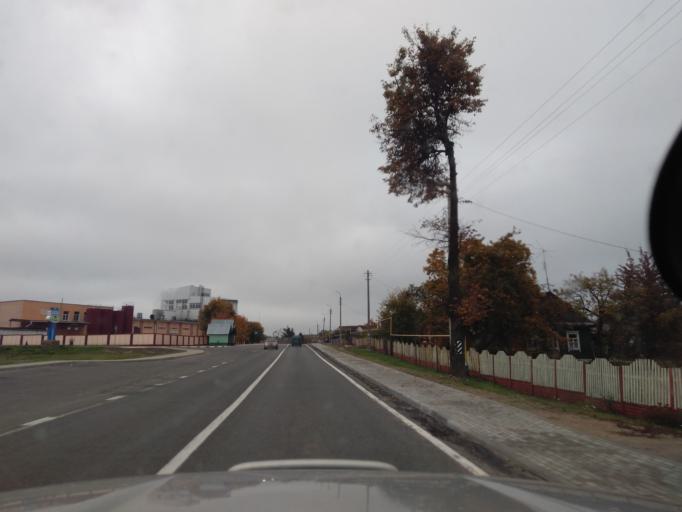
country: BY
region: Minsk
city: Kapyl'
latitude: 53.1410
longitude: 27.0898
